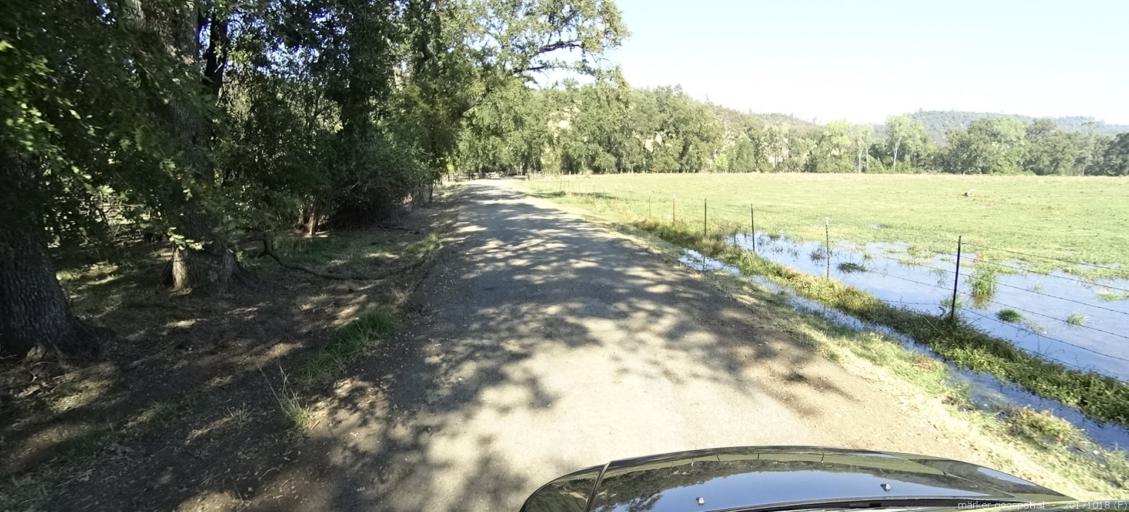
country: US
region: California
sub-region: Shasta County
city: Shingletown
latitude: 40.5617
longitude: -122.0377
